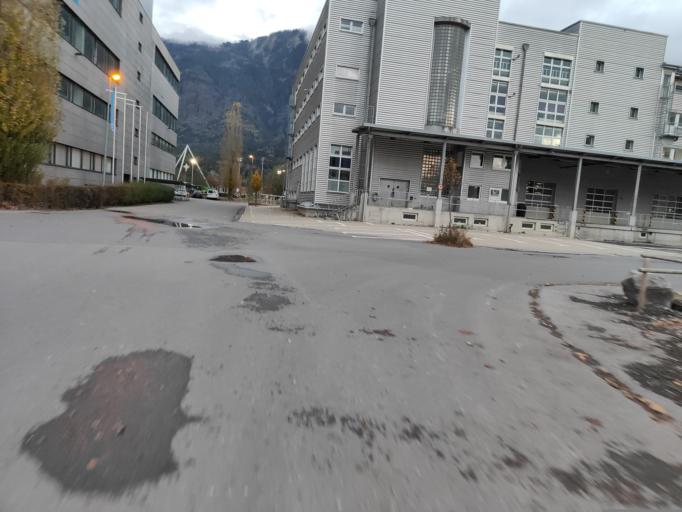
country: LI
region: Eschen
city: Eschen
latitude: 47.2071
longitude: 9.5347
